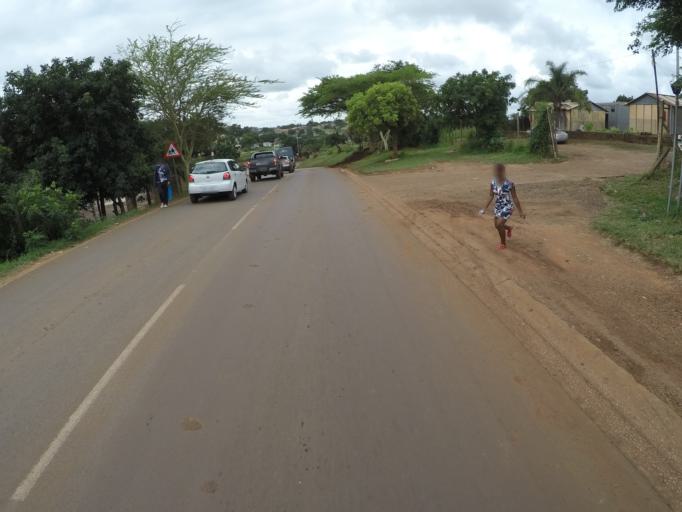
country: ZA
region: KwaZulu-Natal
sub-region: uThungulu District Municipality
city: Empangeni
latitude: -28.7747
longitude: 31.8653
